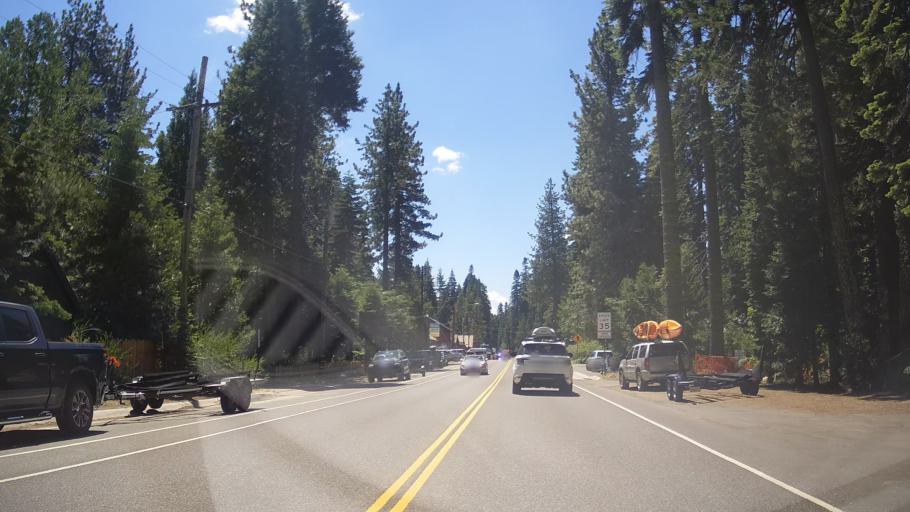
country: US
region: California
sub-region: Placer County
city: Tahoma
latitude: 39.0836
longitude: -120.1592
